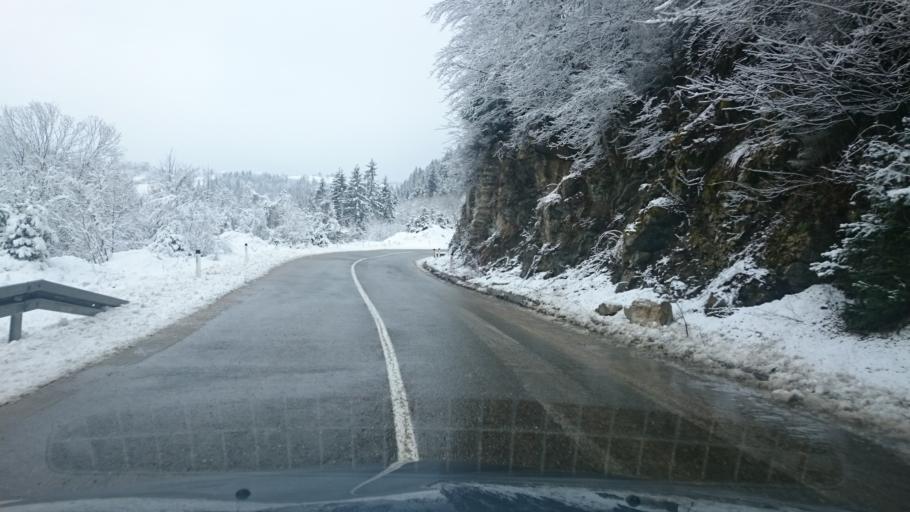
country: BA
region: Republika Srpska
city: Skender Vakuf
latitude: 44.4683
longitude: 17.3762
